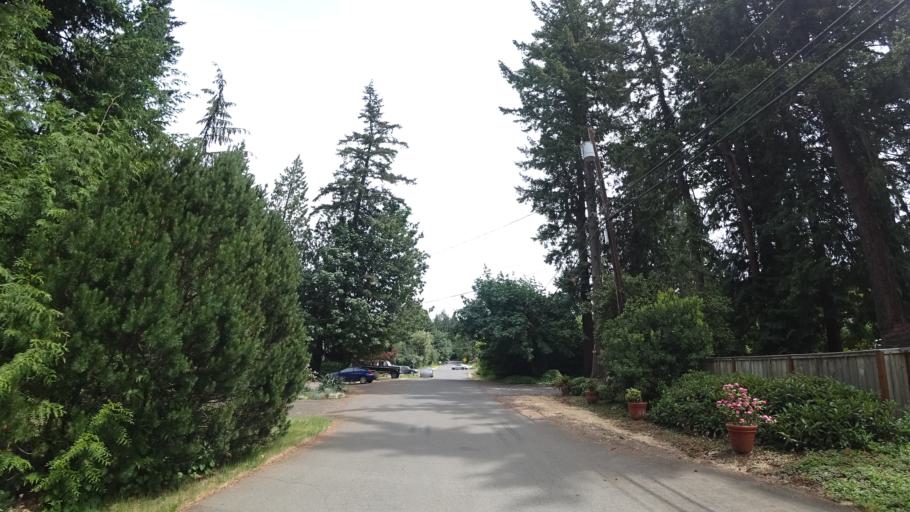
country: US
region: Oregon
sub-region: Washington County
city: Metzger
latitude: 45.4493
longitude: -122.7600
